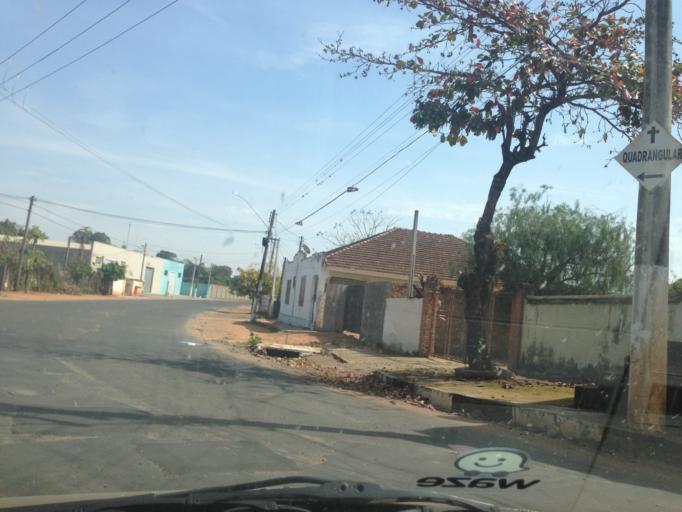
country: BR
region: Sao Paulo
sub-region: Casa Branca
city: Casa Branca
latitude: -21.7698
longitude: -47.0917
